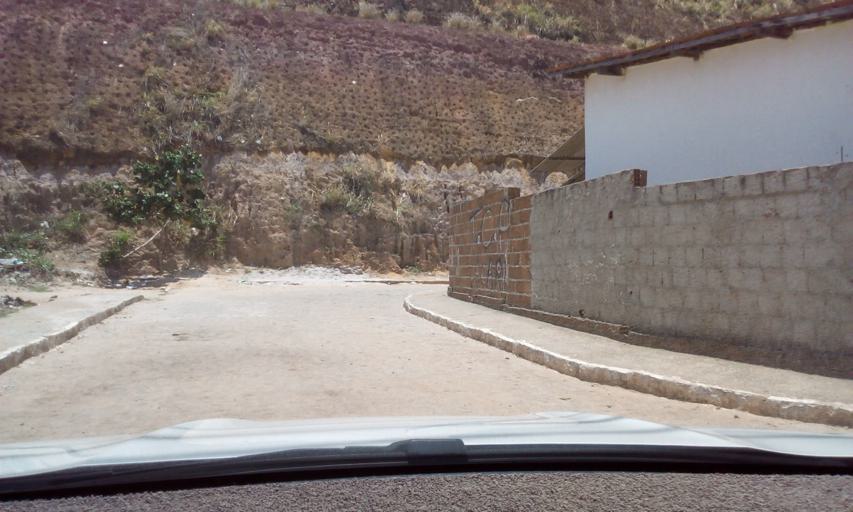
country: BR
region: Paraiba
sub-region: Joao Pessoa
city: Joao Pessoa
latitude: -7.1481
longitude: -34.8275
